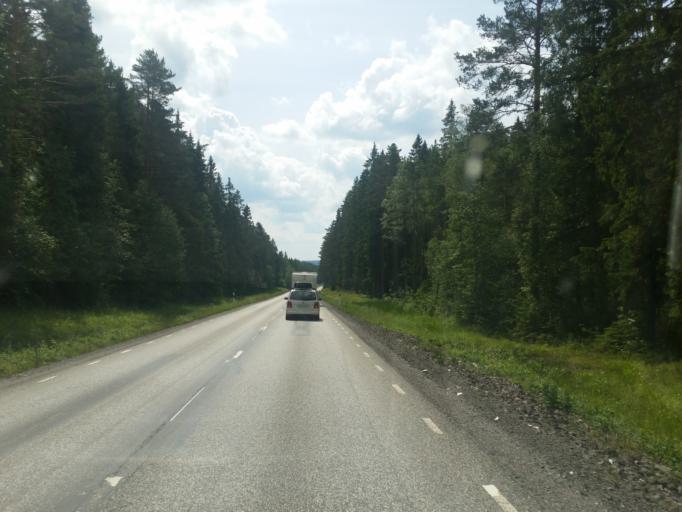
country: SE
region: OErebro
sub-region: Ljusnarsbergs Kommun
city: Kopparberg
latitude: 59.9075
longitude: 15.0214
